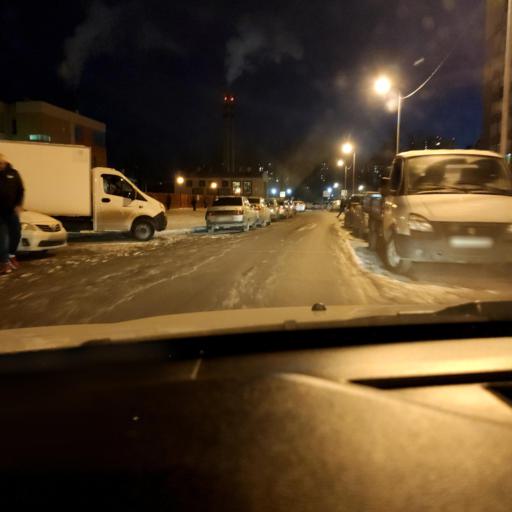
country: RU
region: Samara
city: Rozhdestveno
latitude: 53.1552
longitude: 50.0784
